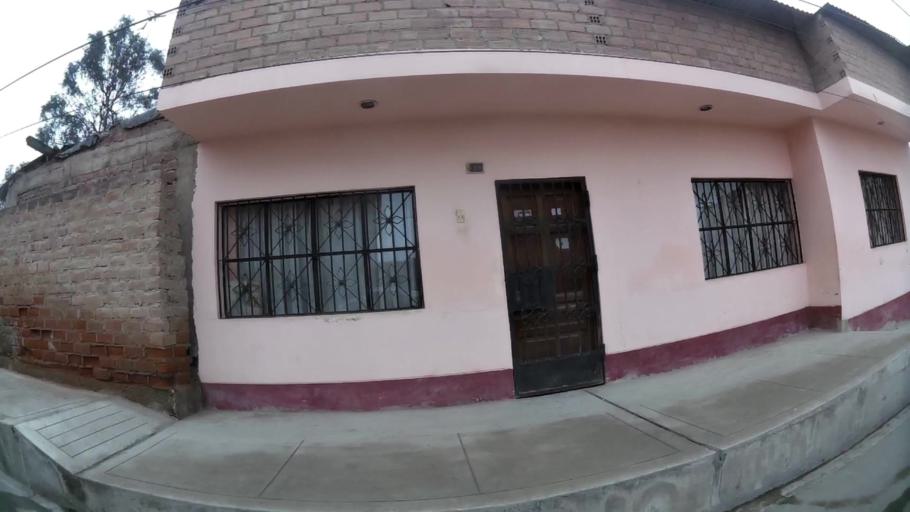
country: PE
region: Lima
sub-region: Lima
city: Surco
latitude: -12.2086
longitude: -76.9109
